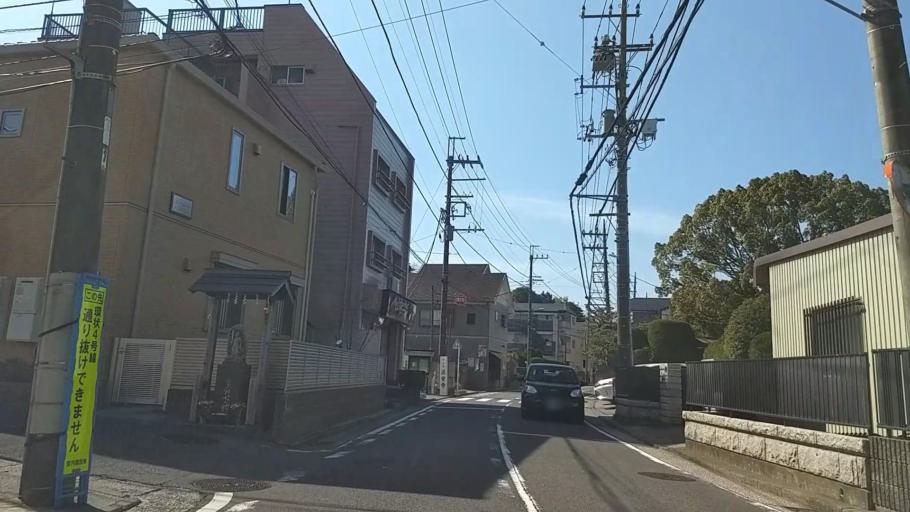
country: JP
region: Kanagawa
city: Kamakura
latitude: 35.3602
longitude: 139.5404
